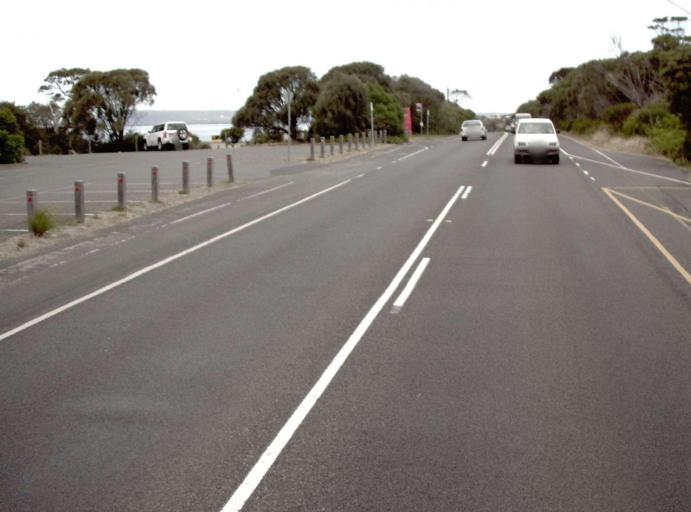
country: AU
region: Victoria
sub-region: Mornington Peninsula
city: Blairgowrie
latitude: -38.3588
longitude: 144.7713
